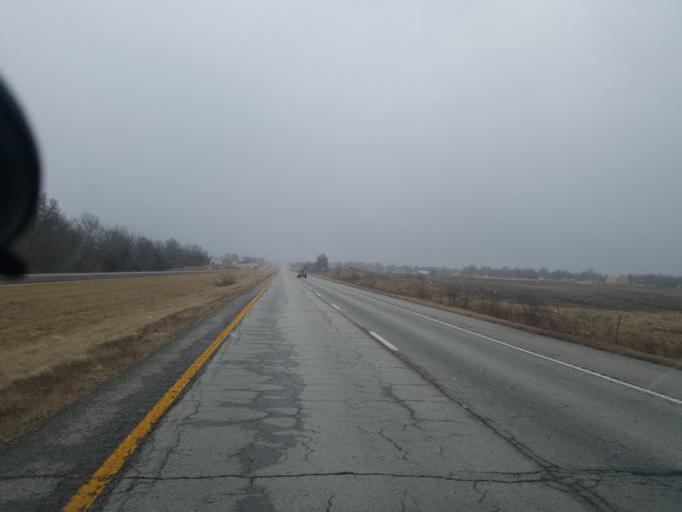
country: US
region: Missouri
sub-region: Macon County
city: La Plata
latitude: 39.9121
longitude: -92.4738
